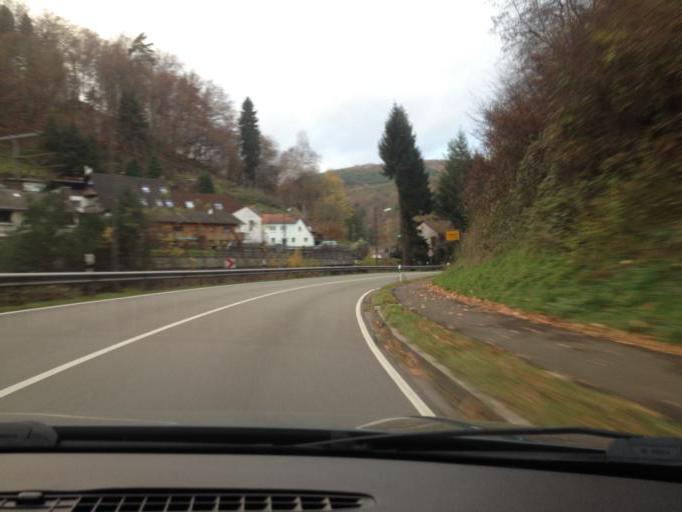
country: DE
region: Rheinland-Pfalz
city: Frankenstein
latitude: 49.4362
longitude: 7.9810
